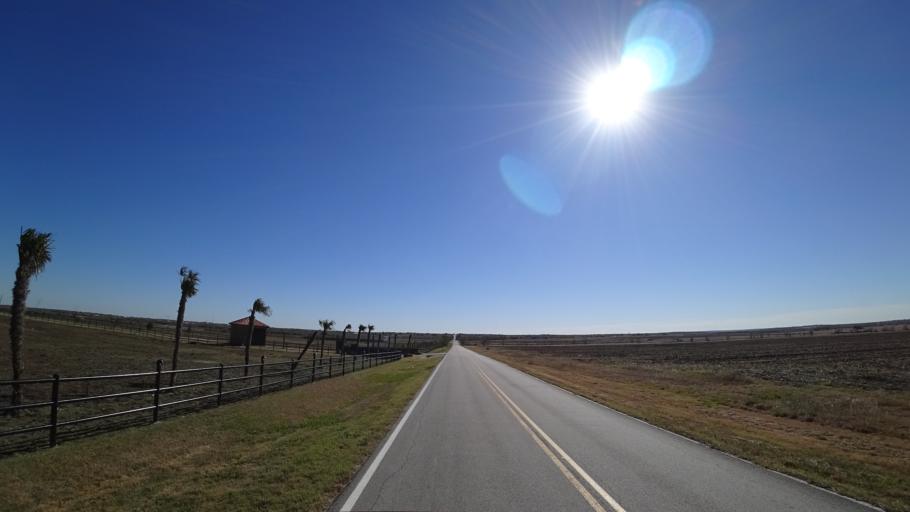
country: US
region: Texas
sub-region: Travis County
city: Garfield
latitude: 30.1012
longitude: -97.6391
